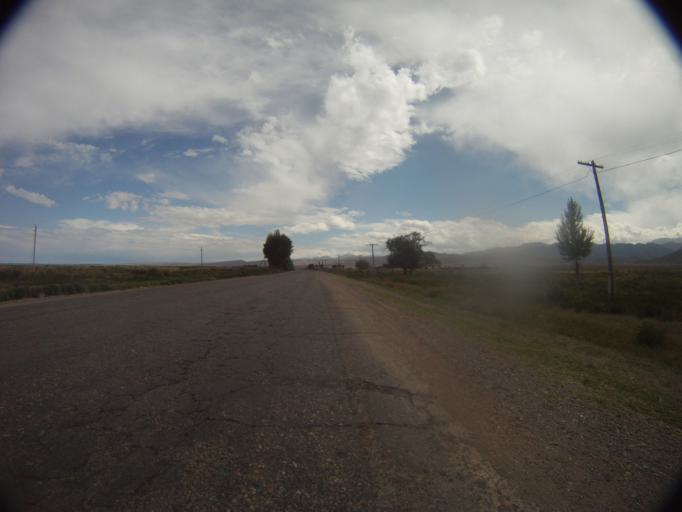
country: KG
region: Ysyk-Koel
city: Balykchy
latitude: 42.3282
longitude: 76.2292
